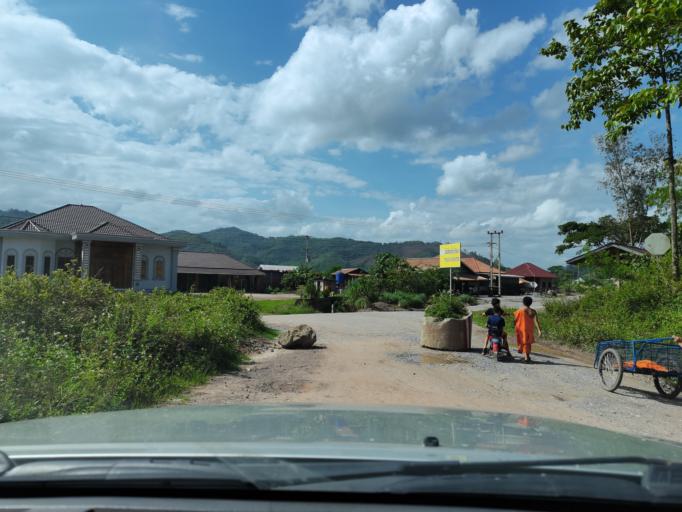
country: LA
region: Loungnamtha
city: Muang Nale
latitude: 20.5912
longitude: 101.0585
